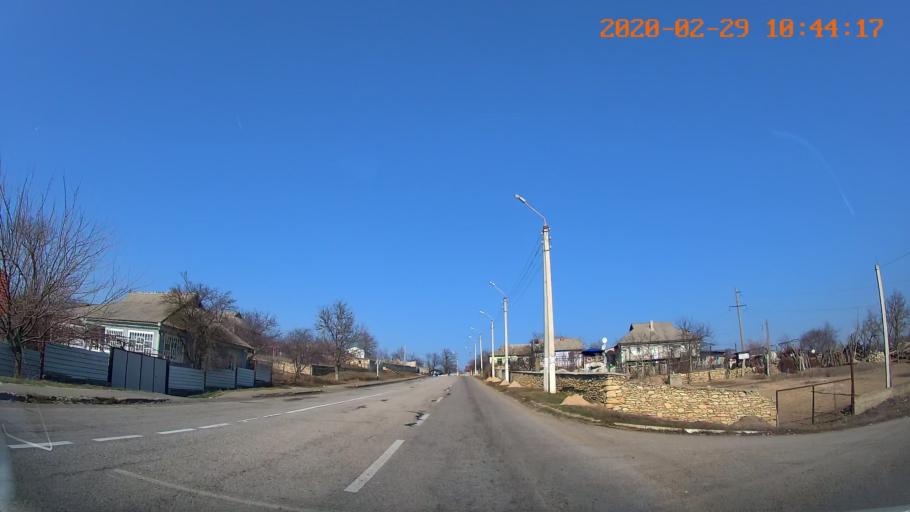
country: MD
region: Telenesti
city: Grigoriopol
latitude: 47.0689
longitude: 29.3964
